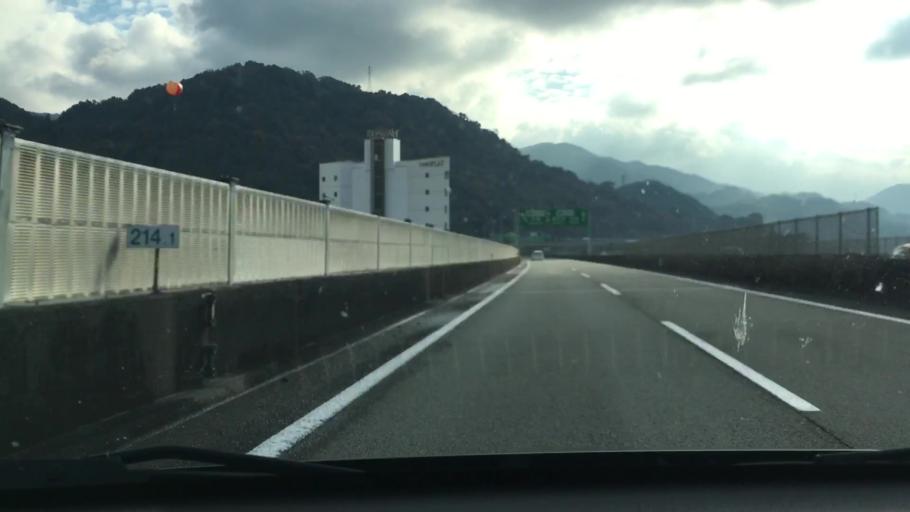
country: JP
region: Kumamoto
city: Yatsushiro
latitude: 32.5080
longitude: 130.6466
